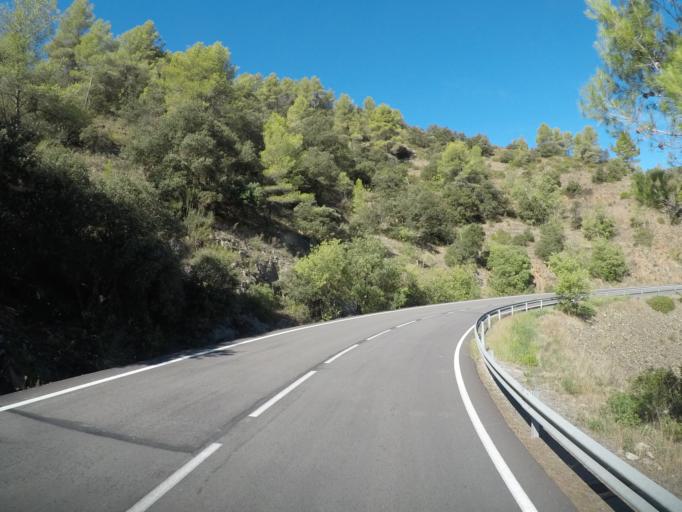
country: ES
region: Catalonia
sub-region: Provincia de Tarragona
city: Falset
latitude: 41.1675
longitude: 0.8071
